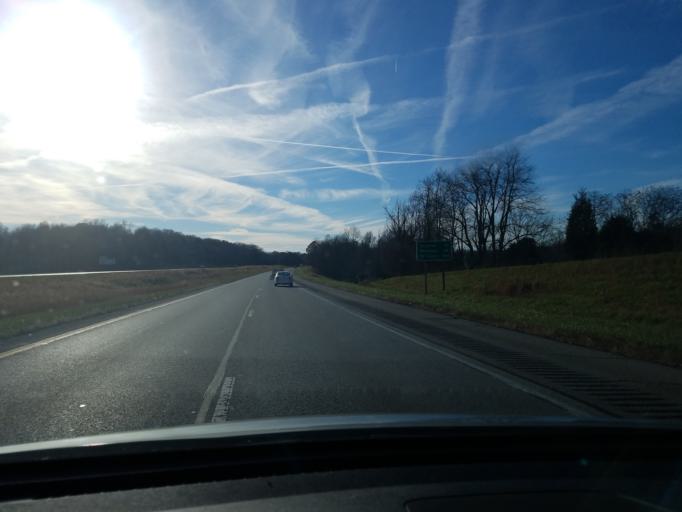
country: US
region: Indiana
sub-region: Floyd County
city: Georgetown
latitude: 38.2579
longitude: -86.0142
